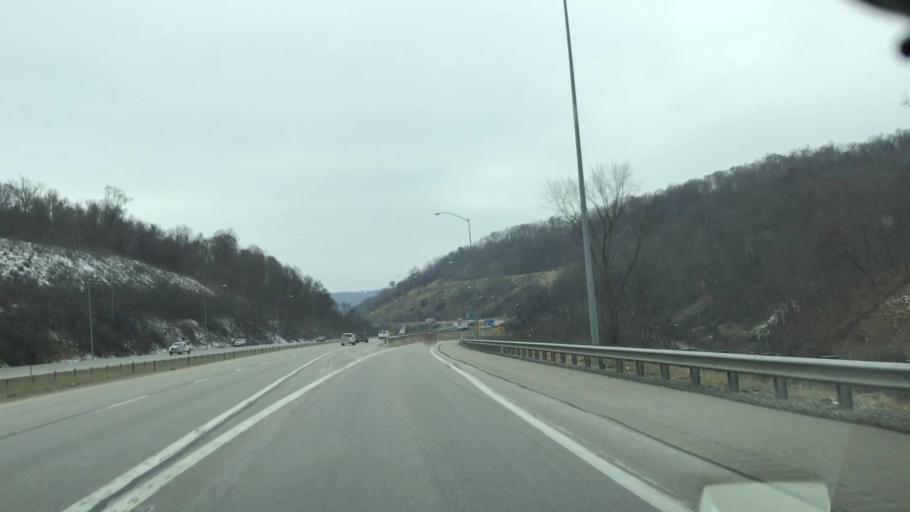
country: US
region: Pennsylvania
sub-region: Allegheny County
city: Emsworth
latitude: 40.5322
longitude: -80.1267
